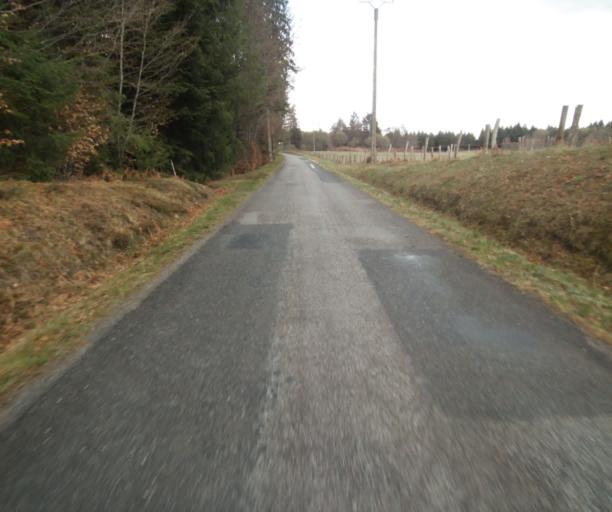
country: FR
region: Limousin
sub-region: Departement de la Correze
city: Correze
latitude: 45.2553
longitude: 1.9184
